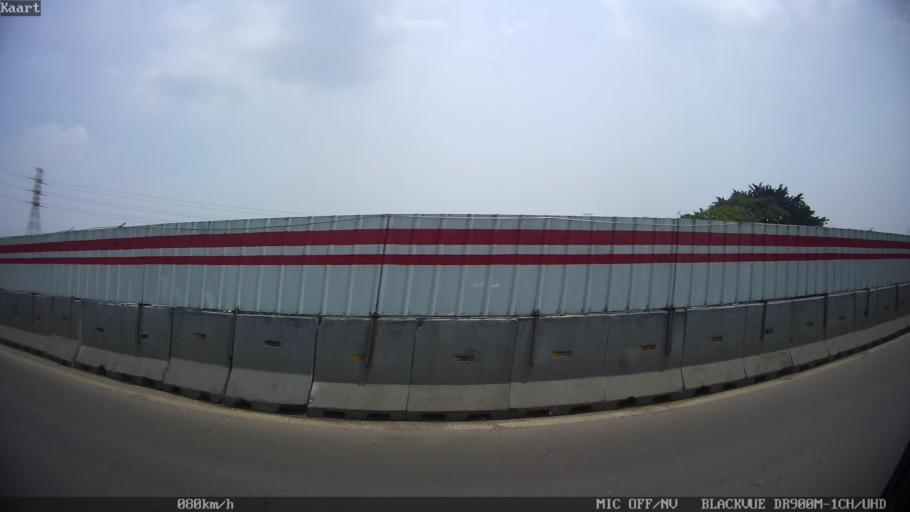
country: ID
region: West Java
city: Kresek
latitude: -6.1700
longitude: 106.3424
